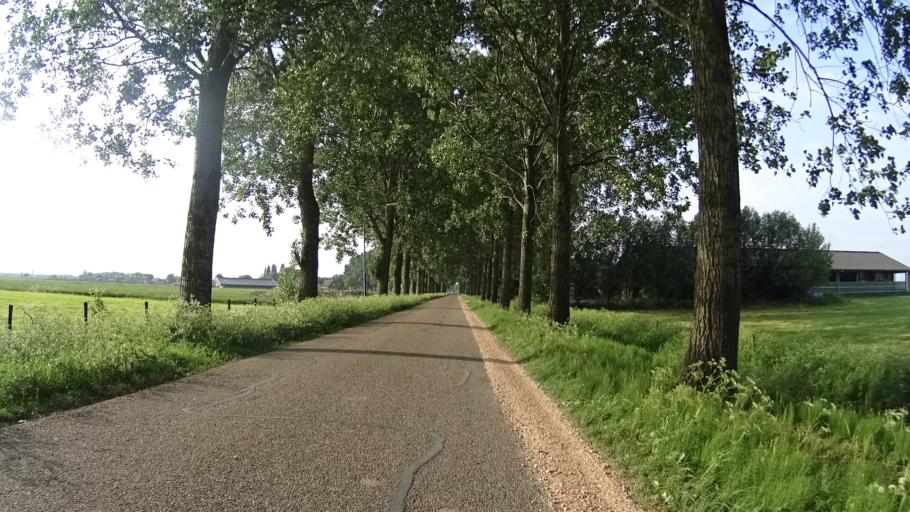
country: NL
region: North Brabant
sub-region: Gemeente Heusden
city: Heusden
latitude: 51.7189
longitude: 5.1610
